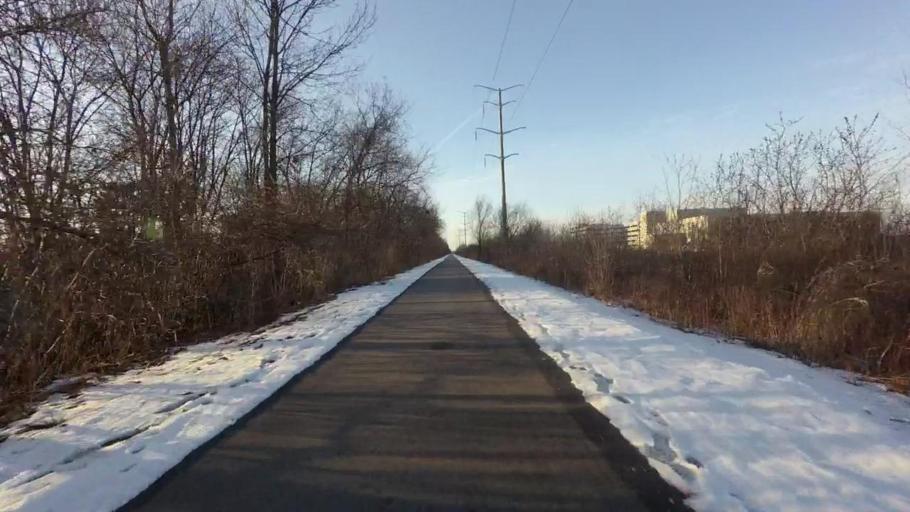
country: US
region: Wisconsin
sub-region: Milwaukee County
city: Glendale
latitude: 43.1232
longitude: -87.9378
